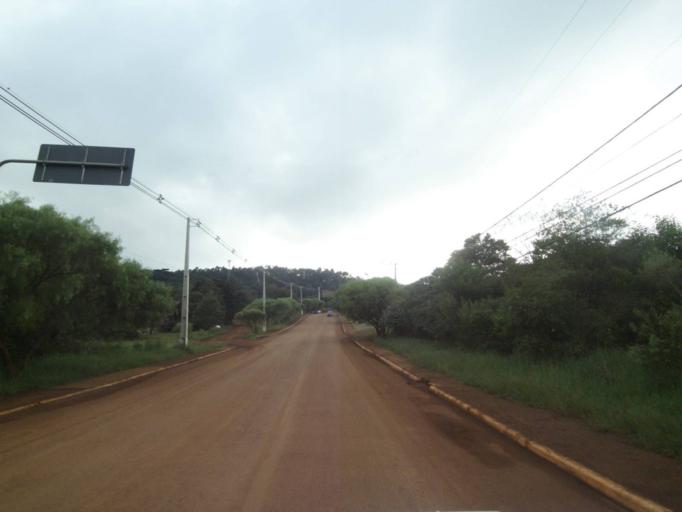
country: BR
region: Parana
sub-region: Pitanga
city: Pitanga
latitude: -24.9402
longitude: -51.8677
